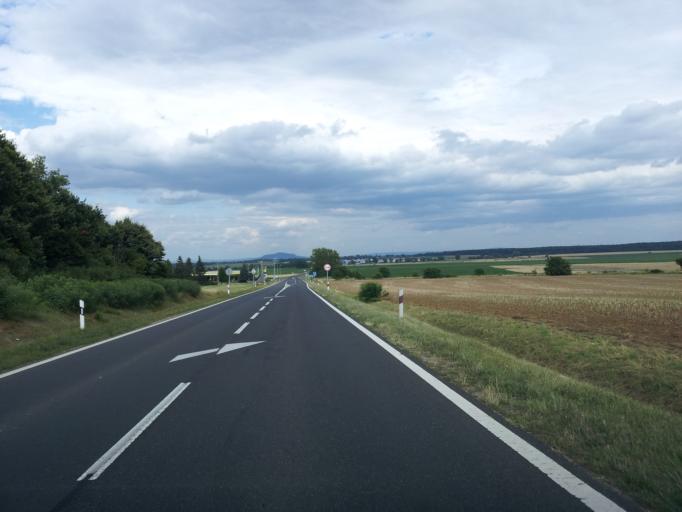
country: HU
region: Vas
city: Janoshaza
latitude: 47.1153
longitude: 17.1133
